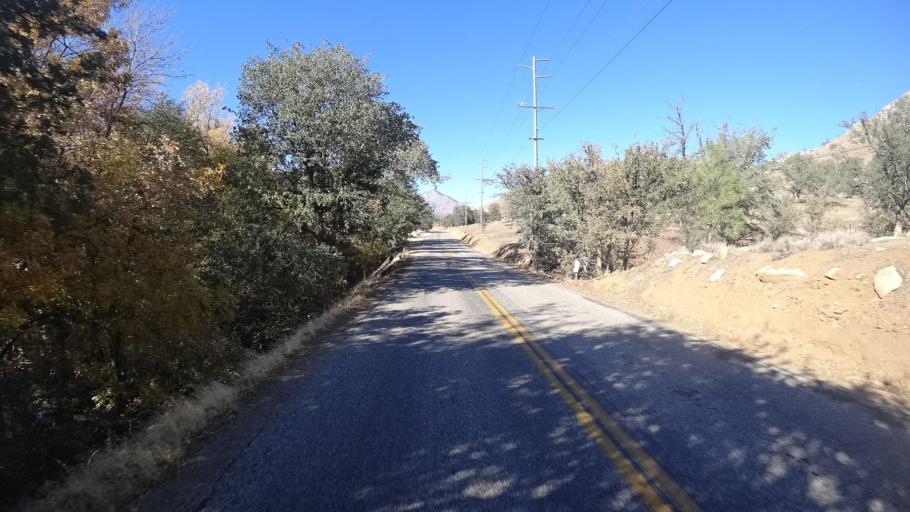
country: US
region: California
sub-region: Kern County
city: Kernville
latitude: 35.7647
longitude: -118.4230
